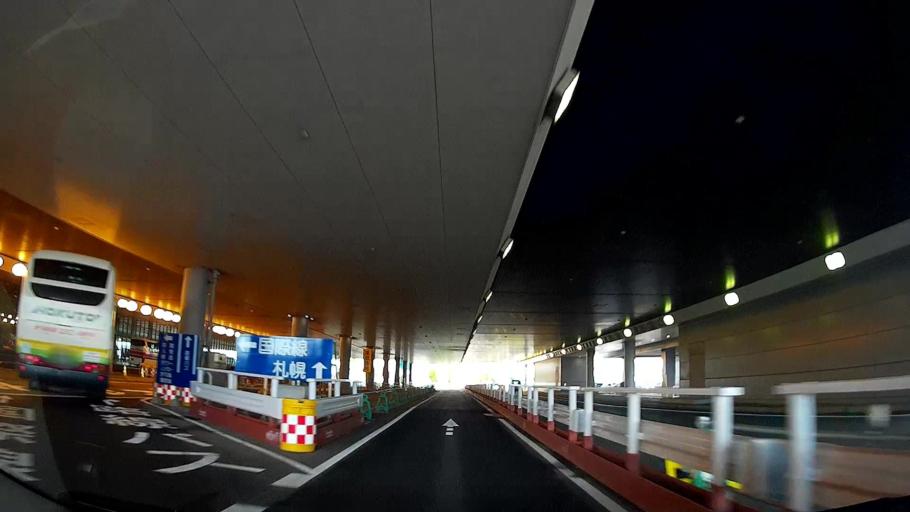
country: JP
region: Hokkaido
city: Chitose
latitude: 42.7868
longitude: 141.6769
